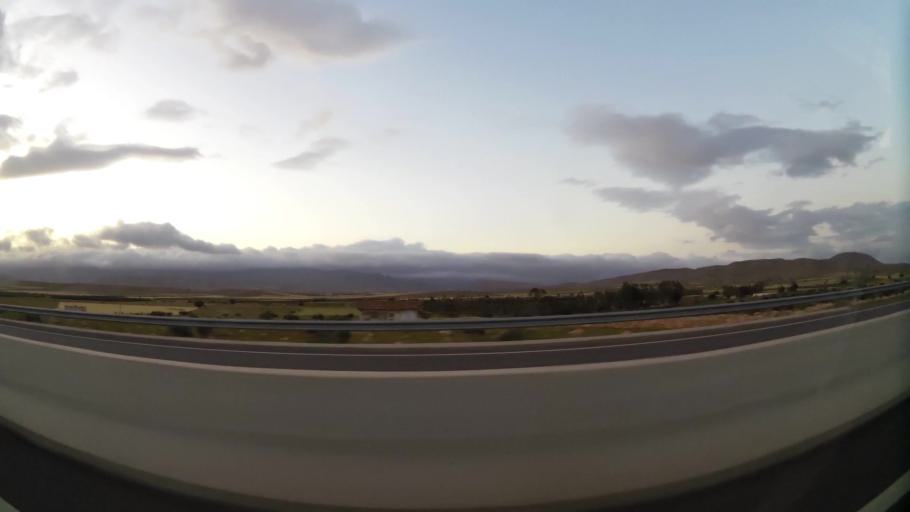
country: MA
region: Oriental
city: El Aioun
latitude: 34.6254
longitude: -2.5077
